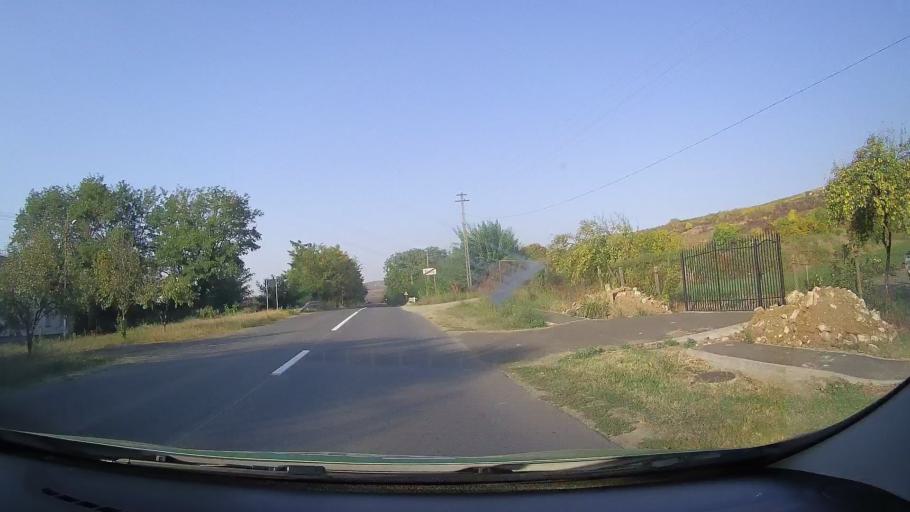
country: RO
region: Arad
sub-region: Comuna Paulis
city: Paulis
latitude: 46.1264
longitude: 21.5993
